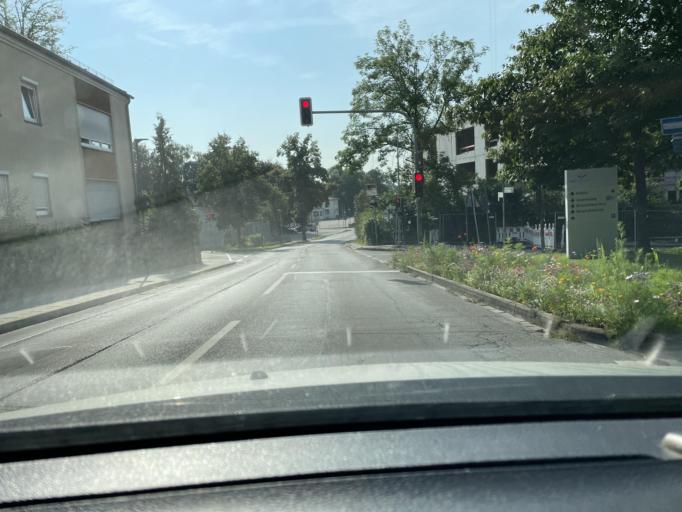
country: DE
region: Bavaria
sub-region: Upper Bavaria
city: Muehldorf
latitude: 48.2439
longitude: 12.5289
